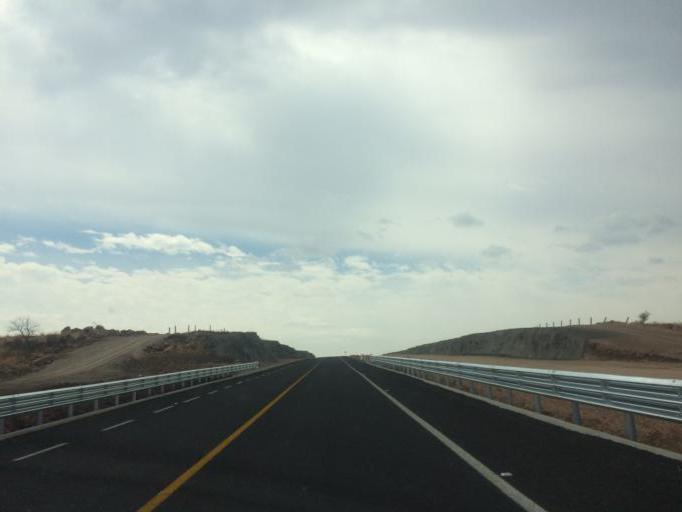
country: MX
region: Guanajuato
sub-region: Leon
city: Ladrilleras del Refugio
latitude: 21.0690
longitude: -101.5384
